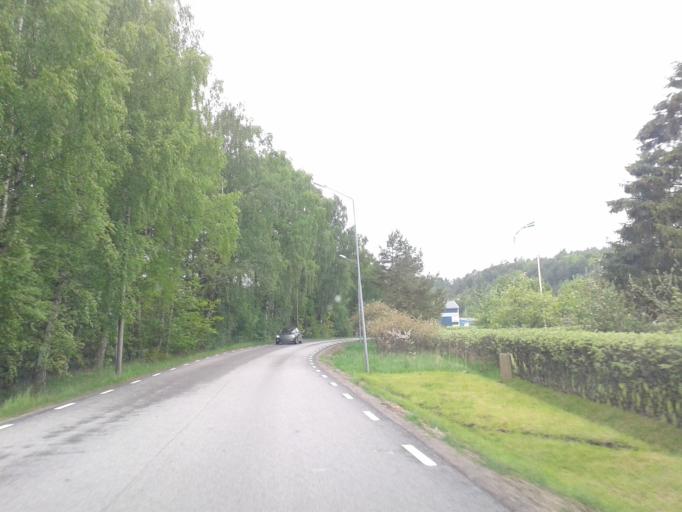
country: SE
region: Vaestra Goetaland
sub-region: Kungalvs Kommun
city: Kode
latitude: 57.8451
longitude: 11.7900
